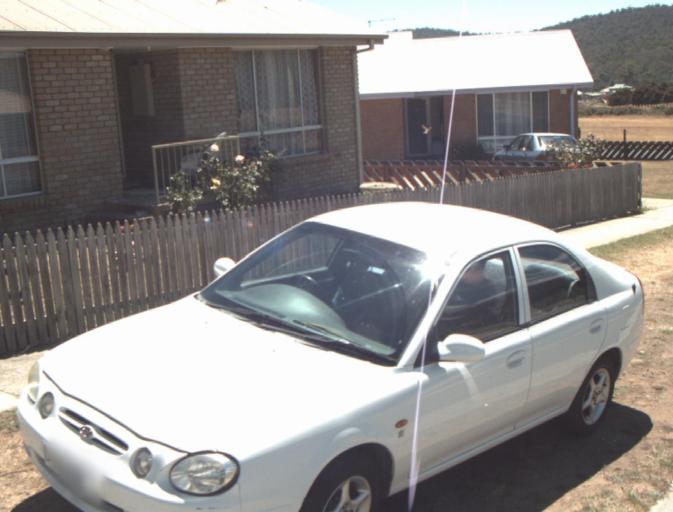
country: AU
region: Tasmania
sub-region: Launceston
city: Mayfield
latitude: -41.3748
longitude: 147.1411
